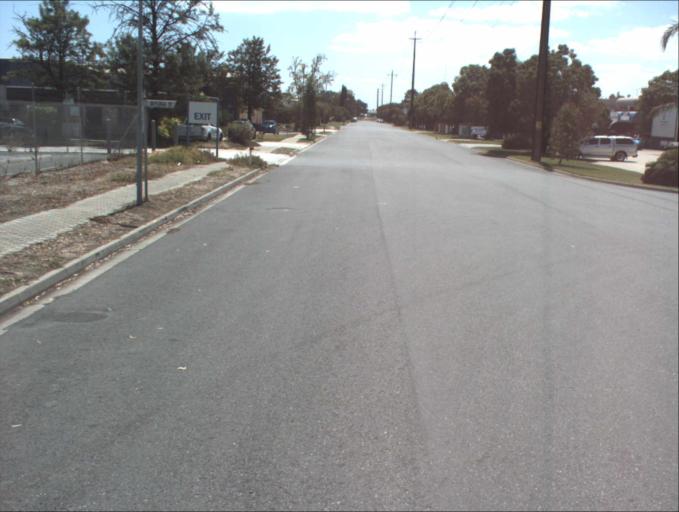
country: AU
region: South Australia
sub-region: Port Adelaide Enfield
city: Blair Athol
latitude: -34.8547
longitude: 138.5699
